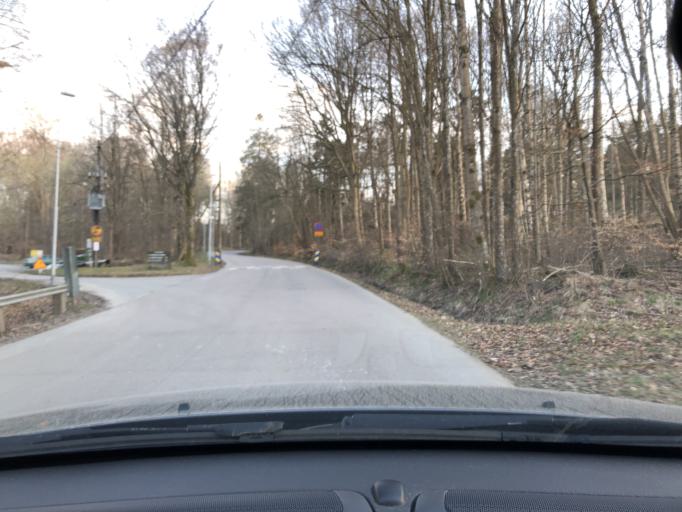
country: SE
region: Vaestra Goetaland
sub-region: Molndal
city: Moelndal
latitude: 57.6946
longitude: 12.0337
